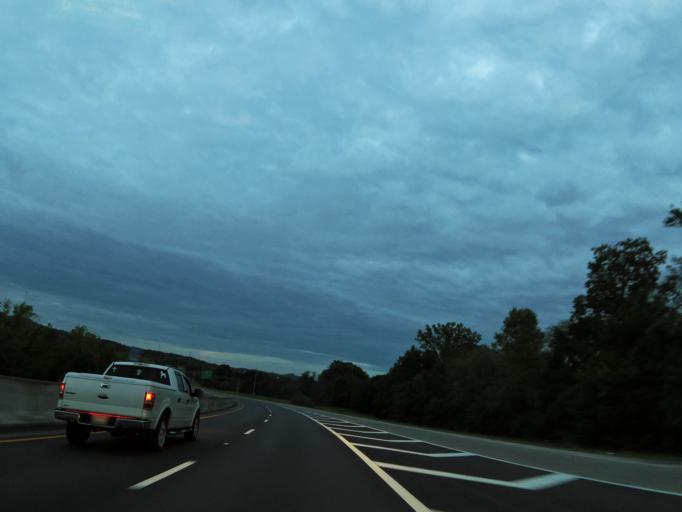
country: US
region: Tennessee
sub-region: Davidson County
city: Nashville
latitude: 36.2290
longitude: -86.8322
